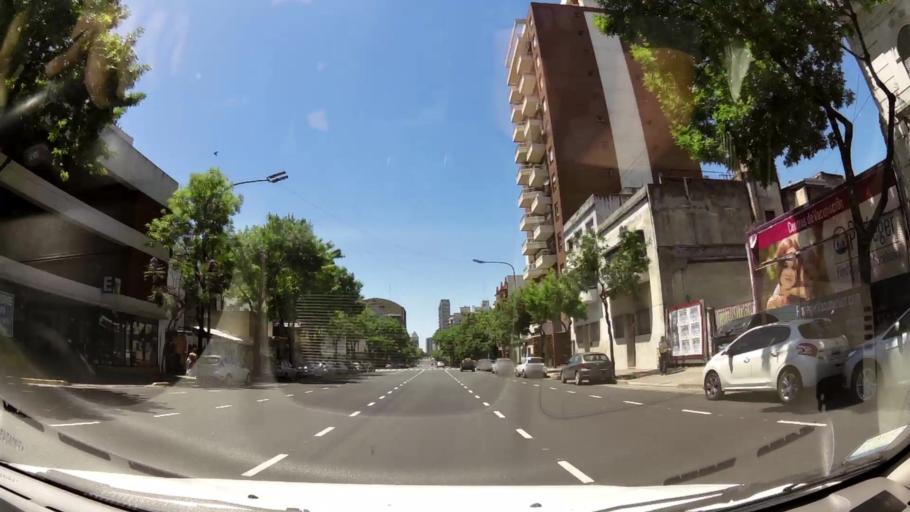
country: AR
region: Buenos Aires F.D.
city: Buenos Aires
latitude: -34.6221
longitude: -58.3781
